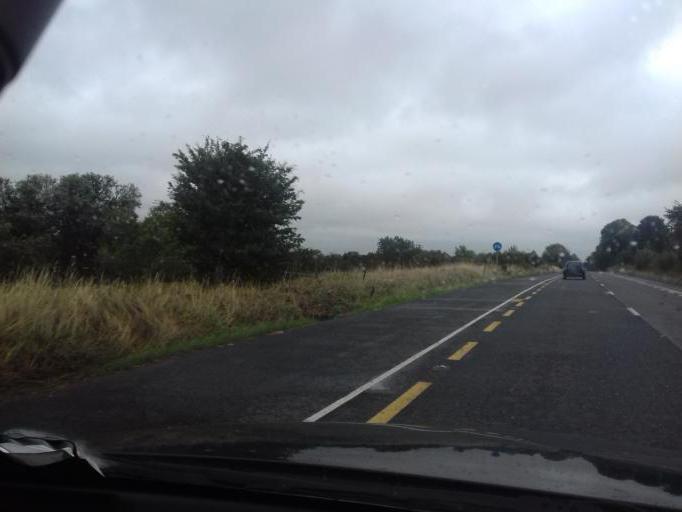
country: IE
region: Leinster
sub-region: County Carlow
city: Bagenalstown
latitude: 52.7517
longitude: -6.9627
